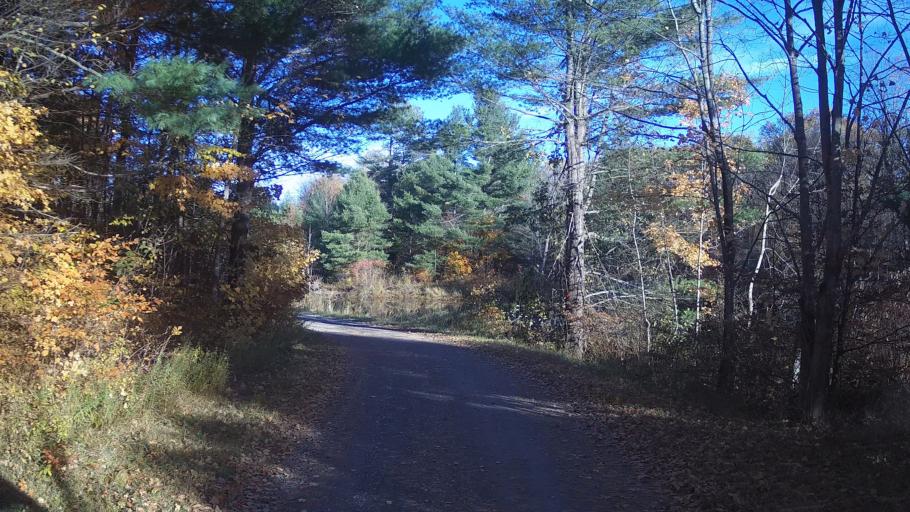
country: CA
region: Ontario
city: Perth
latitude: 44.7360
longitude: -76.4191
